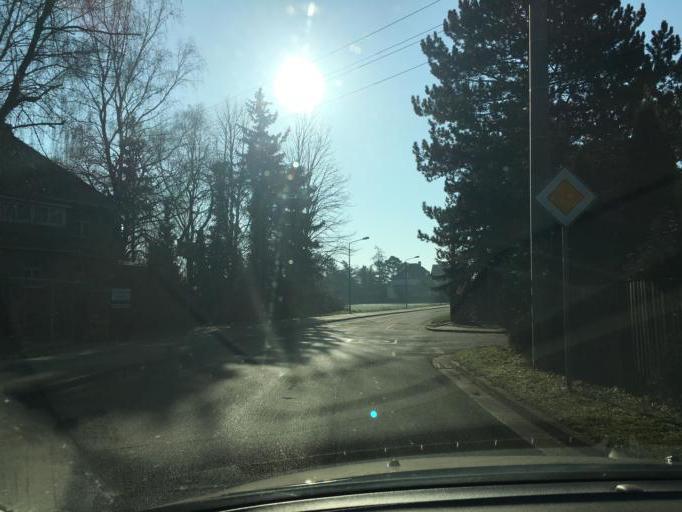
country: DE
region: Saxony
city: Grossposna
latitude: 51.2980
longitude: 12.4539
